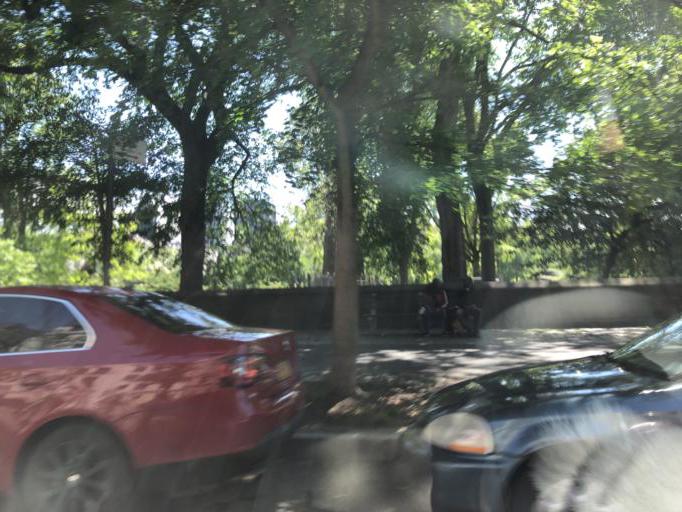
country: US
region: New York
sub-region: New York County
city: Manhattan
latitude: 40.7978
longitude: -73.9515
